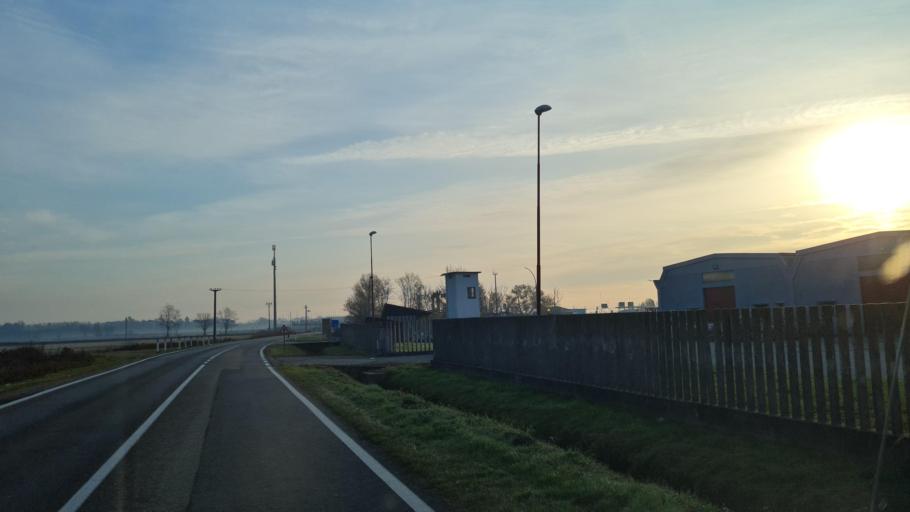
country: IT
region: Piedmont
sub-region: Provincia di Vercelli
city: Balocco
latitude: 45.4504
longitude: 8.2895
